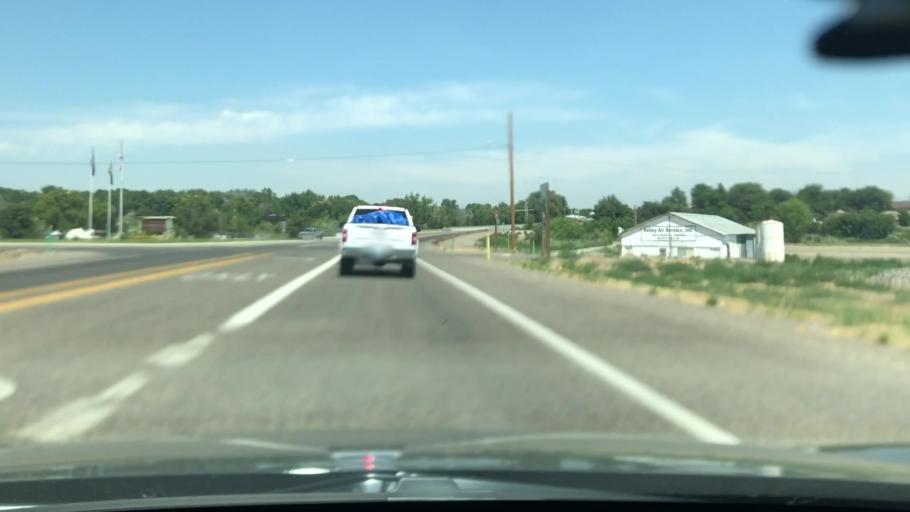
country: US
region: Idaho
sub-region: Owyhee County
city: Homedale
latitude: 43.6170
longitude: -116.9258
